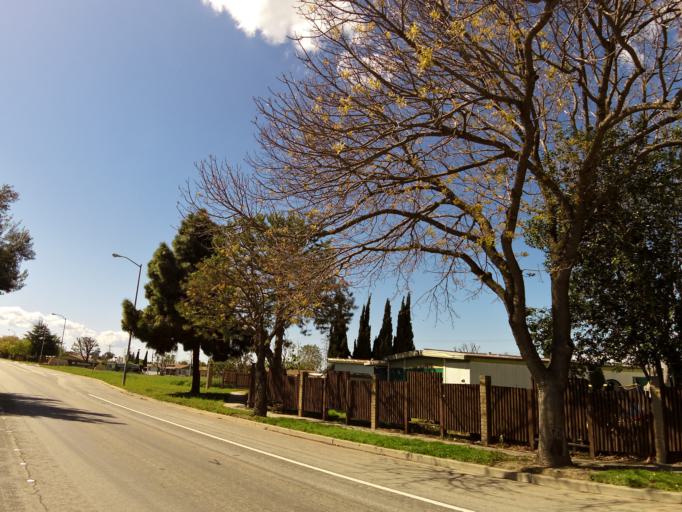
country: US
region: California
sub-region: Alameda County
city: Fremont
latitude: 37.5109
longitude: -121.9566
